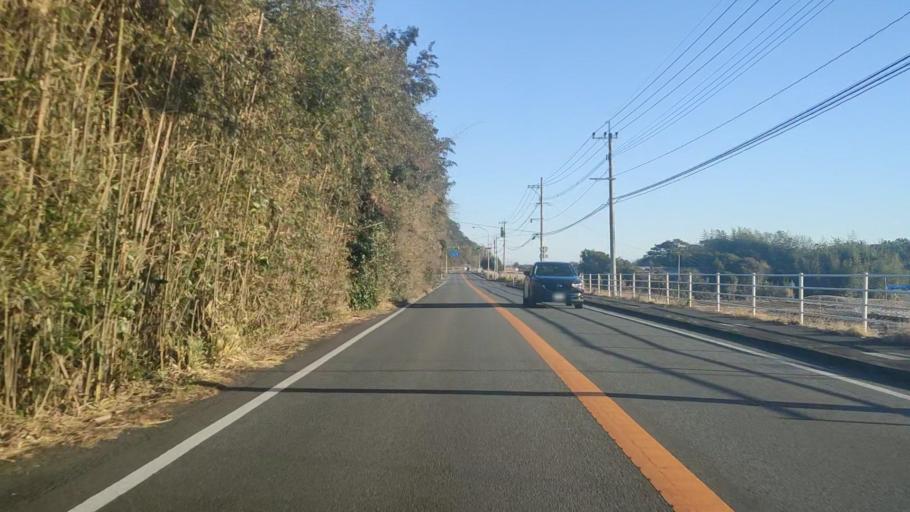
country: JP
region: Miyazaki
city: Takanabe
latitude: 32.1021
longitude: 131.5212
